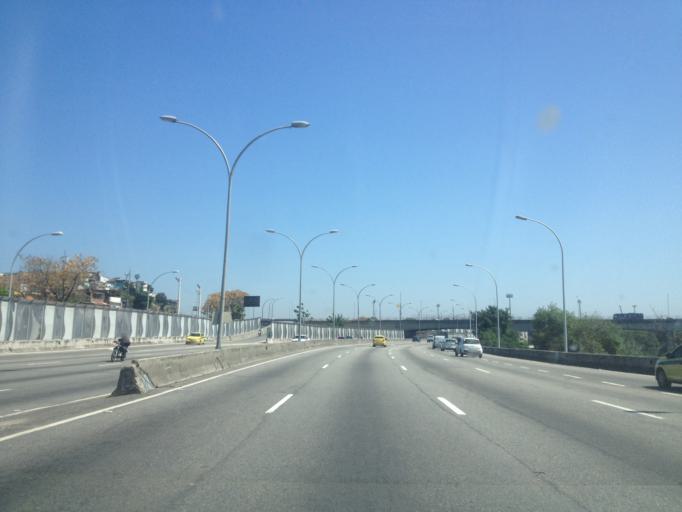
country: BR
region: Rio de Janeiro
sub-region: Rio De Janeiro
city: Rio de Janeiro
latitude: -22.8634
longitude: -43.2351
